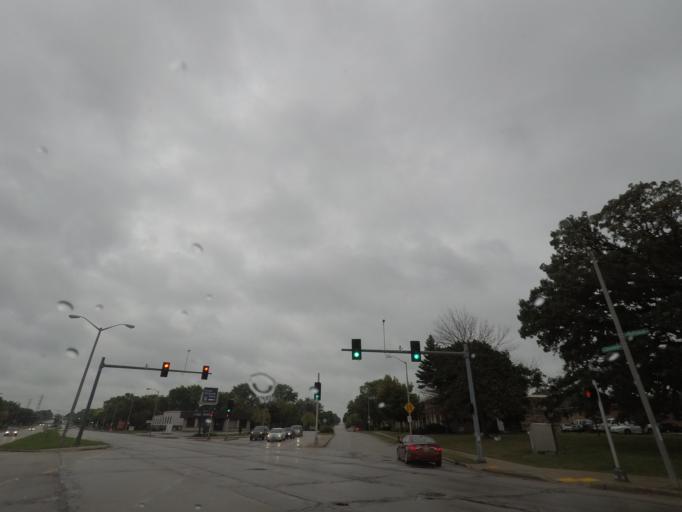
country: US
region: Wisconsin
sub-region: Milwaukee County
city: West Allis
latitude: 42.9953
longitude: -88.0442
